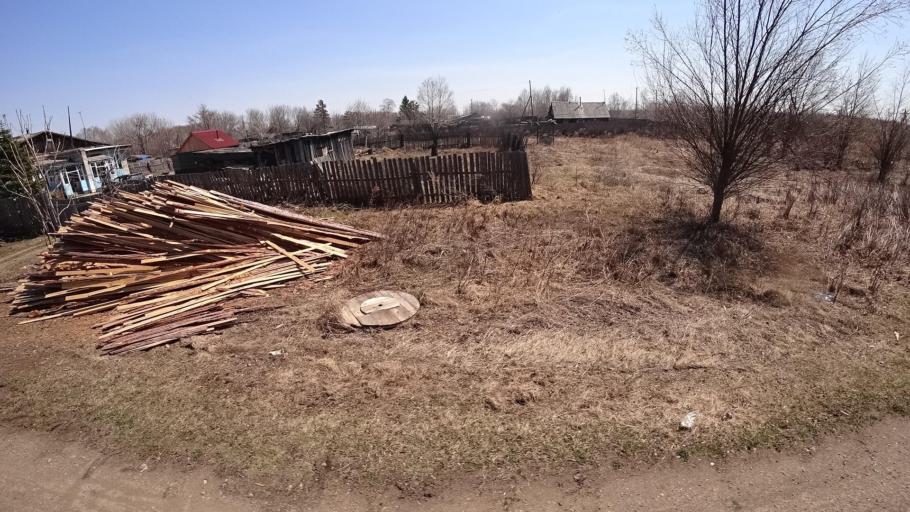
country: RU
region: Khabarovsk Krai
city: Khurba
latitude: 50.4041
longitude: 136.8704
